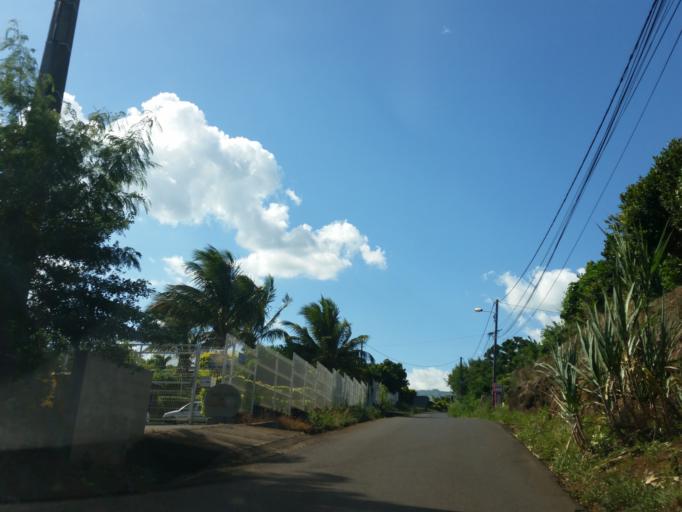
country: RE
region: Reunion
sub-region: Reunion
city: Saint-Pierre
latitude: -21.3201
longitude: 55.5024
